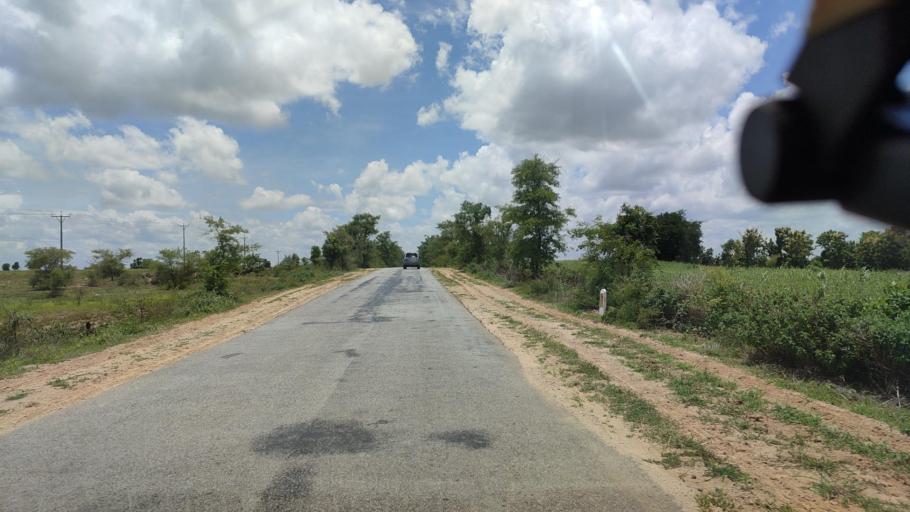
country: MM
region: Magway
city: Taungdwingyi
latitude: 20.2012
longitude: 95.3590
